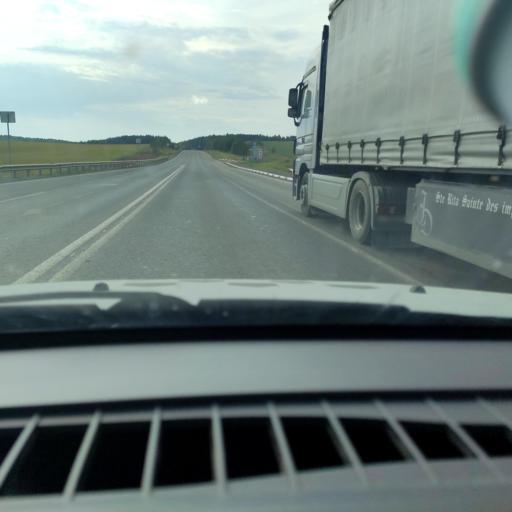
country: RU
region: Perm
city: Siva
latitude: 58.4141
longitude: 54.4666
